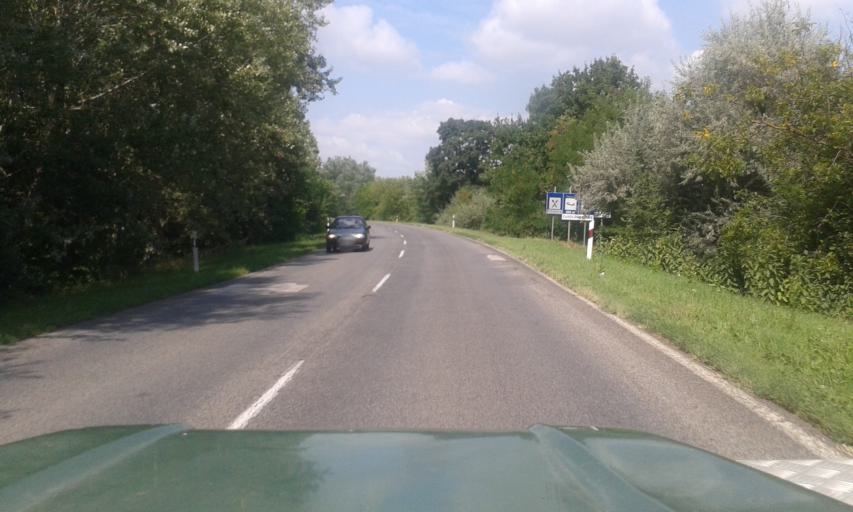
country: HU
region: Csongrad
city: Szatymaz
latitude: 46.3408
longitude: 20.0655
